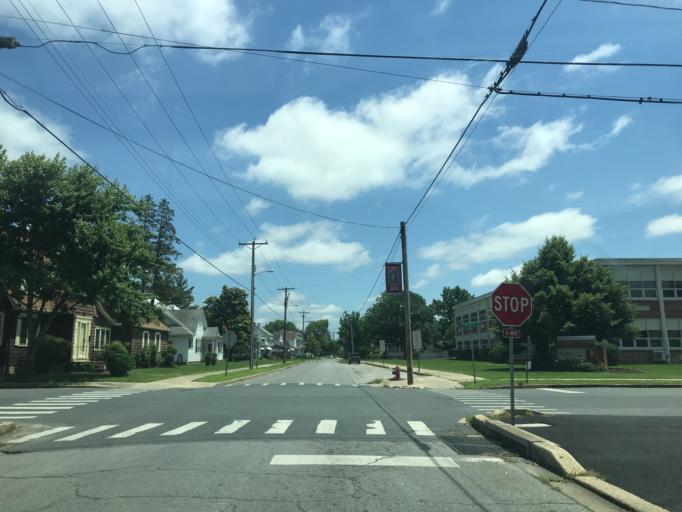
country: US
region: Maryland
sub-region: Caroline County
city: Federalsburg
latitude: 38.6909
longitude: -75.7808
